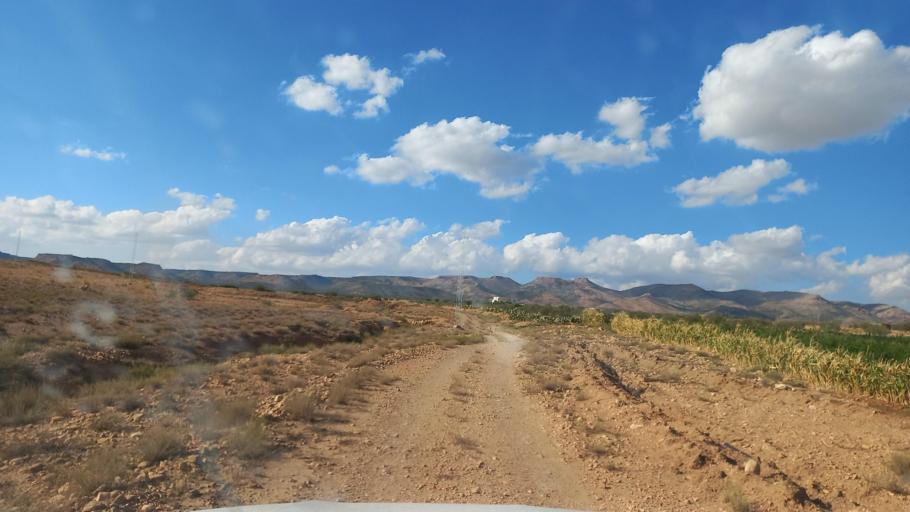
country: TN
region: Al Qasrayn
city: Sbiba
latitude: 35.3990
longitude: 9.0312
